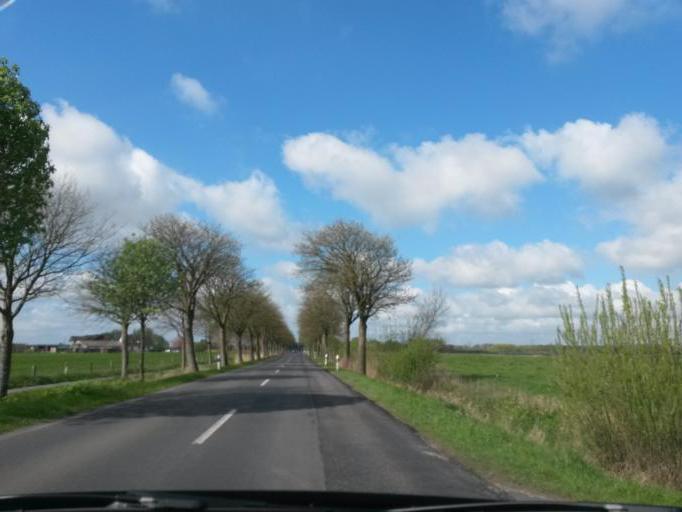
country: DE
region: Schleswig-Holstein
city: Holm
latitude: 53.6146
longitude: 9.6567
